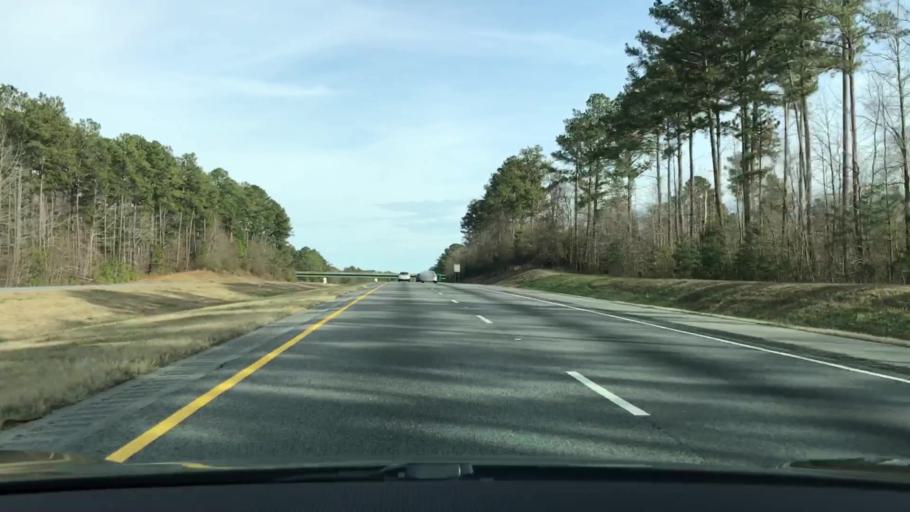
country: US
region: Georgia
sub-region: Walton County
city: Social Circle
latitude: 33.6116
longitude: -83.7242
